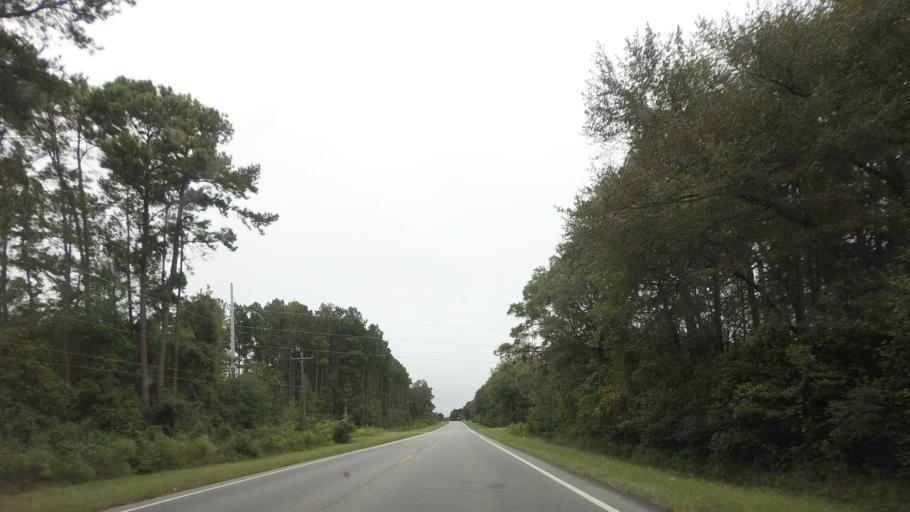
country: US
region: Georgia
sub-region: Berrien County
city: Nashville
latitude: 31.2270
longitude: -83.2474
